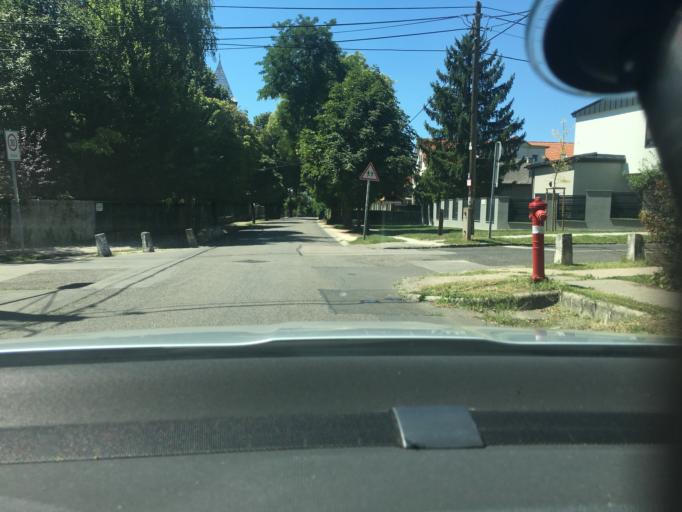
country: HU
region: Budapest
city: Budapest XVI. keruelet
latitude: 47.5141
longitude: 19.1722
